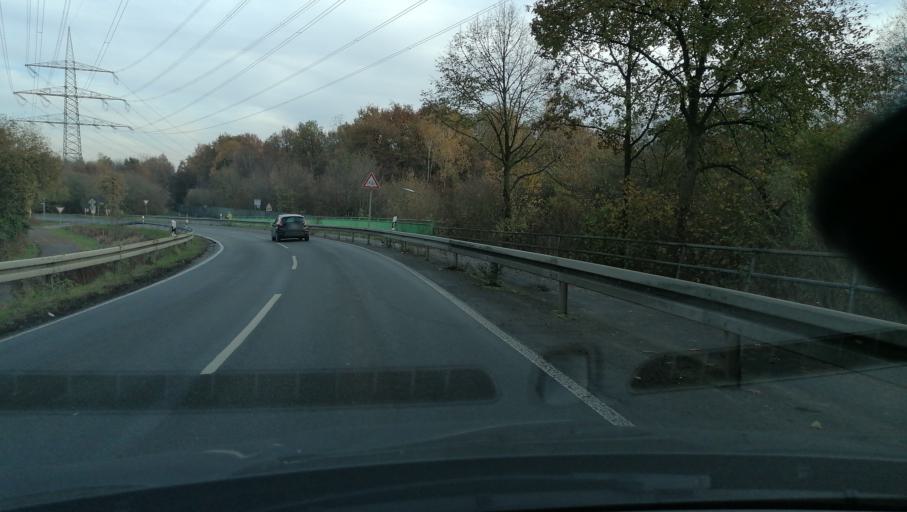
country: DE
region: North Rhine-Westphalia
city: Castrop-Rauxel
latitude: 51.5828
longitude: 7.2917
